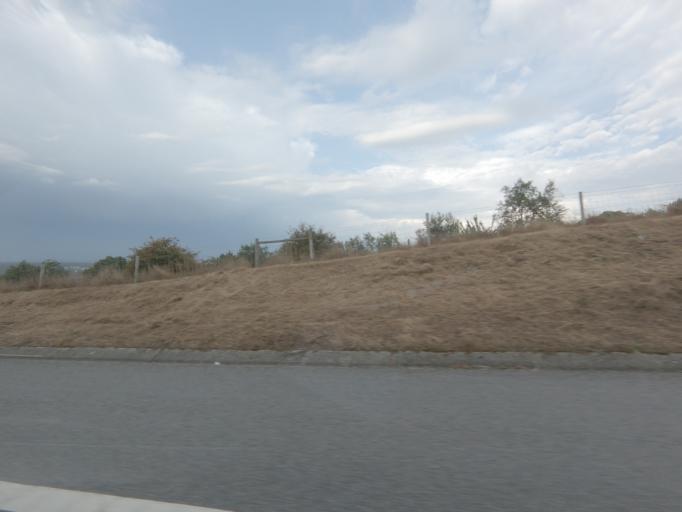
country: PT
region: Viseu
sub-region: Viseu
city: Campo
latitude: 40.7346
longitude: -7.9227
